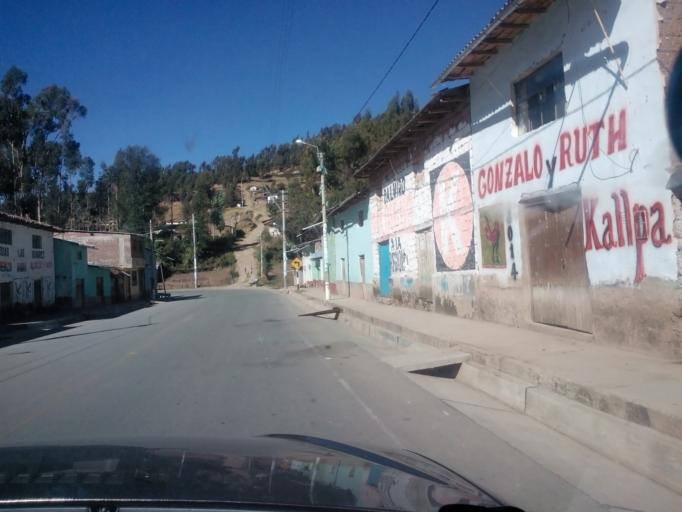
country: PE
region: Apurimac
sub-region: Provincia de Andahuaylas
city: Talavera
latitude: -13.6582
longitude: -73.4930
